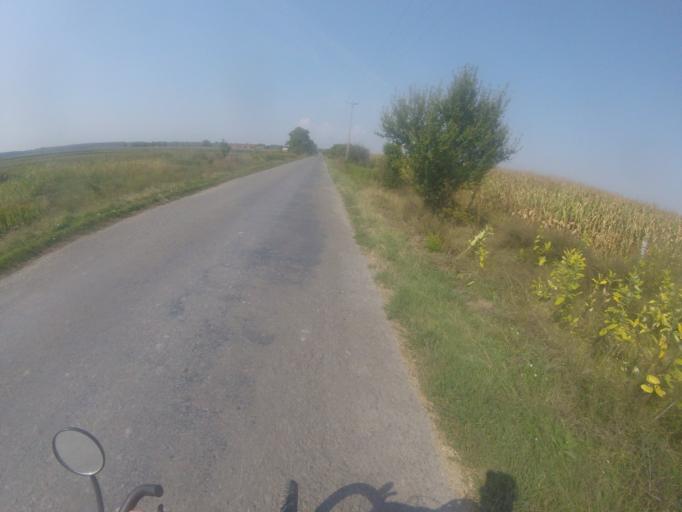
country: HU
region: Bacs-Kiskun
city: Ersekcsanad
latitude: 46.2562
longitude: 18.9436
